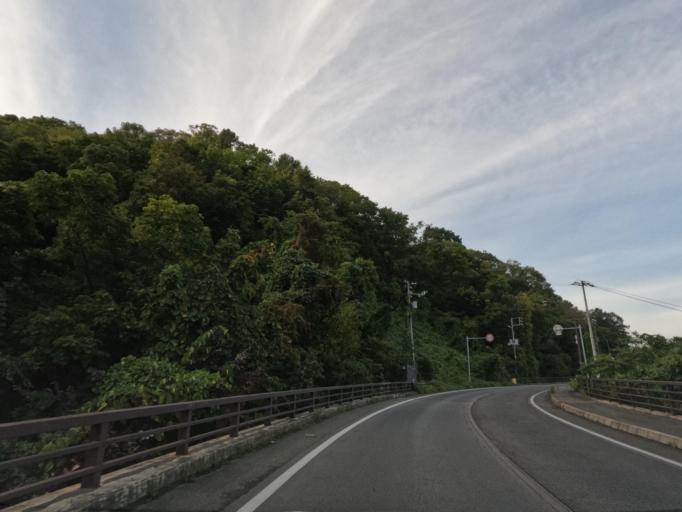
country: JP
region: Hokkaido
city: Date
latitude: 42.5267
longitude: 140.8614
